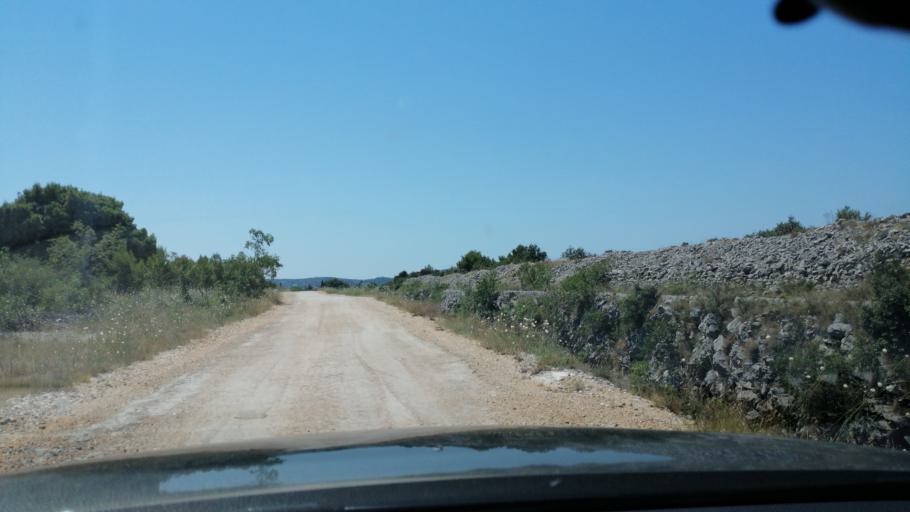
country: HR
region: Sibensko-Kniniska
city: Murter
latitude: 43.8488
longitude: 15.6283
